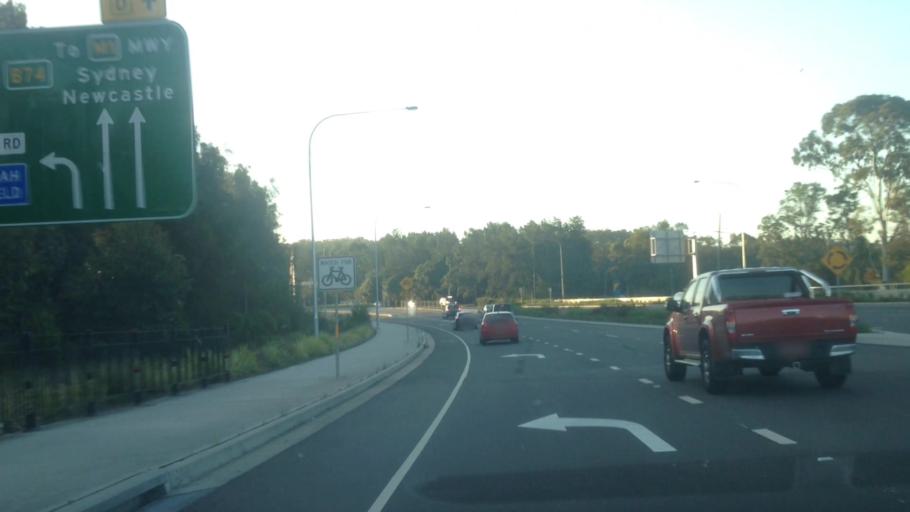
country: AU
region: New South Wales
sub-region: Wyong Shire
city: Chittaway Bay
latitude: -33.3080
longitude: 151.4175
